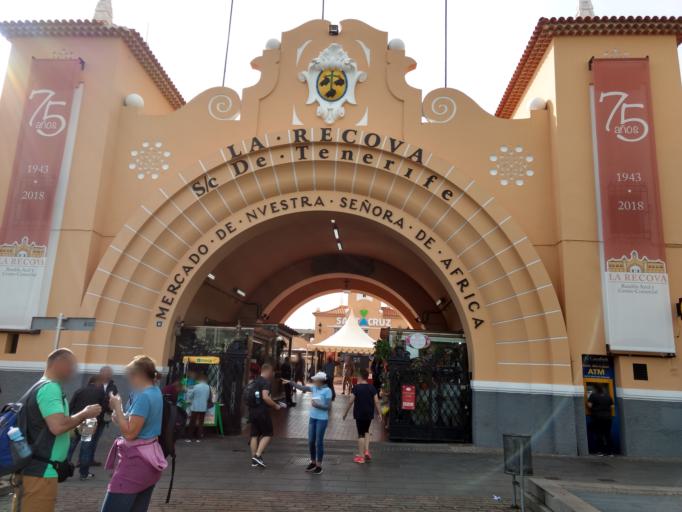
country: ES
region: Canary Islands
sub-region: Provincia de Santa Cruz de Tenerife
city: Santa Cruz de Tenerife
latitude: 28.4635
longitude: -16.2518
